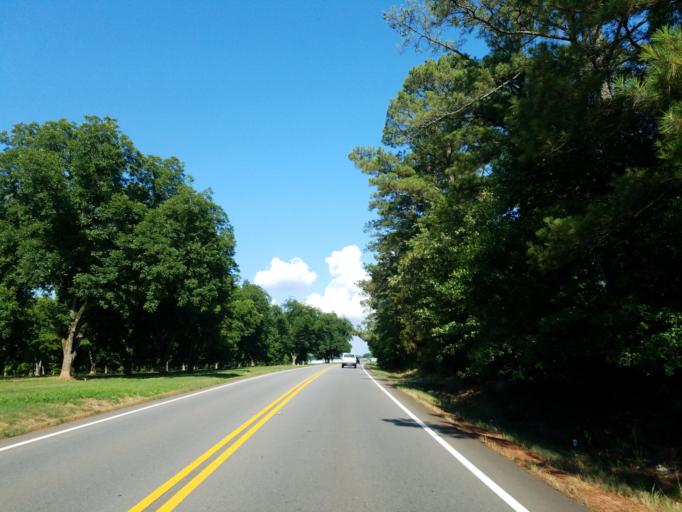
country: US
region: Georgia
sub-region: Peach County
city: Fort Valley
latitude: 32.5567
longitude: -83.8364
